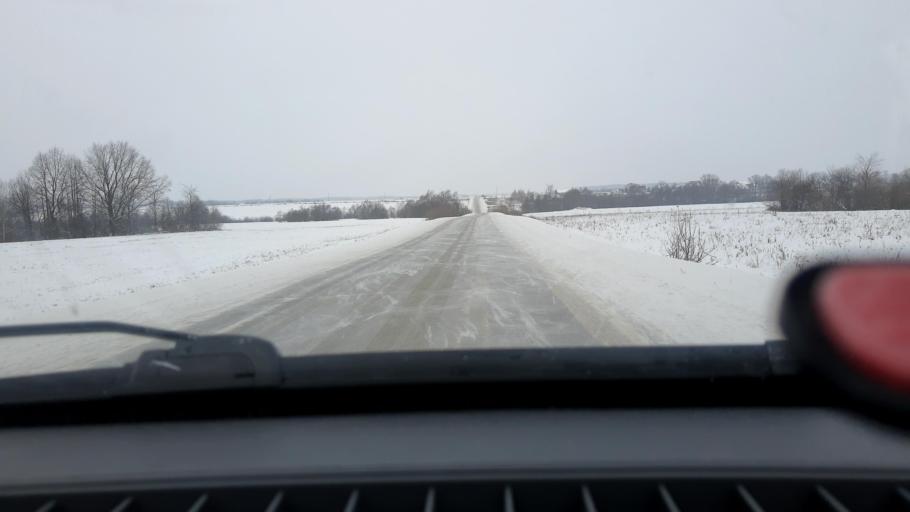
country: RU
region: Bashkortostan
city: Iglino
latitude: 54.7037
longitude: 56.4084
